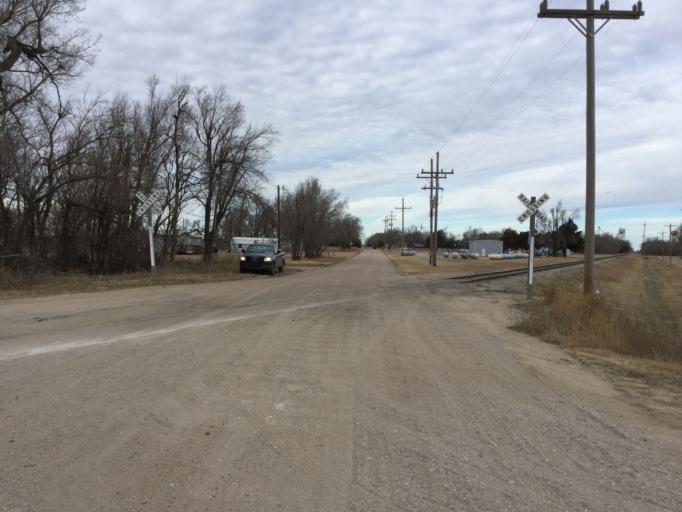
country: US
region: Kansas
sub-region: Rice County
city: Sterling
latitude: 38.2027
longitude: -98.1938
